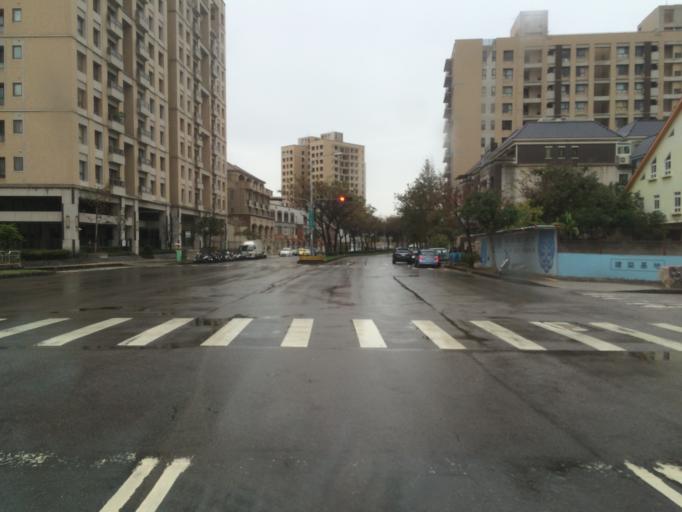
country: TW
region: Taiwan
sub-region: Taichung City
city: Taichung
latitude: 24.1764
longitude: 120.7128
